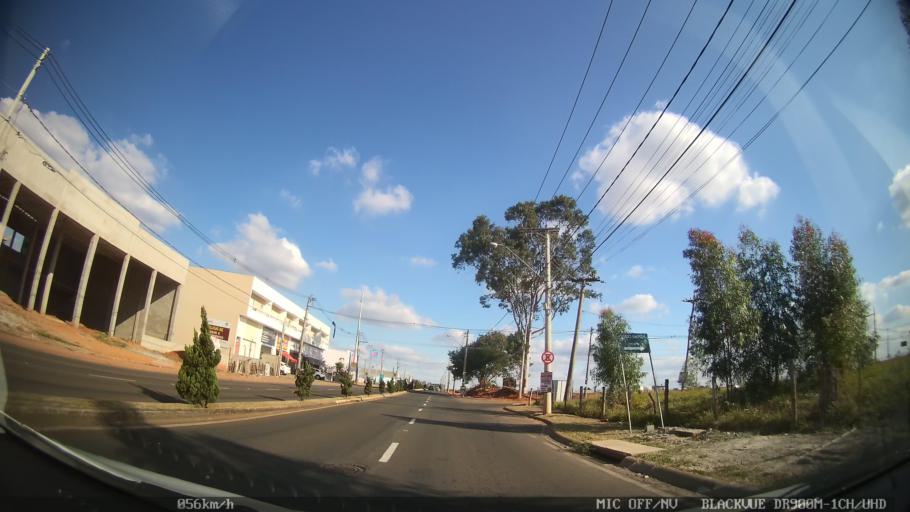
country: BR
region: Sao Paulo
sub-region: Nova Odessa
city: Nova Odessa
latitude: -22.7960
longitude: -47.3152
